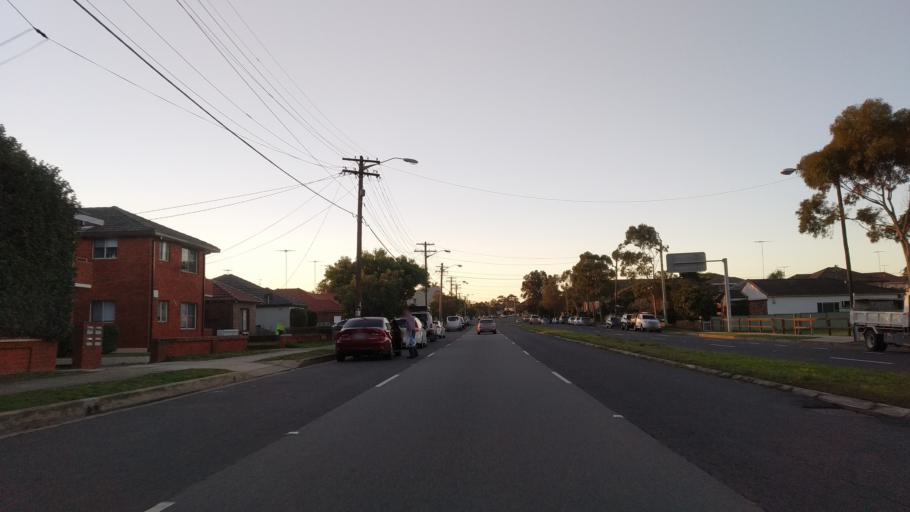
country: AU
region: New South Wales
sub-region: Randwick
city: Maroubra
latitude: -33.9662
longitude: 151.2311
